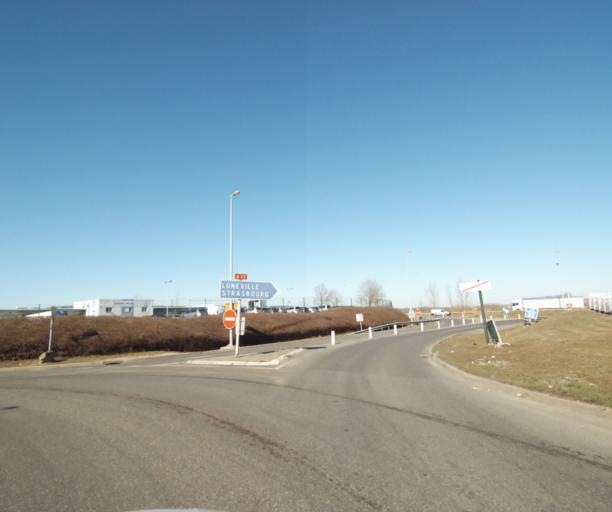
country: FR
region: Lorraine
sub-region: Departement de Meurthe-et-Moselle
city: Fleville-devant-Nancy
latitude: 48.6172
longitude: 6.2100
